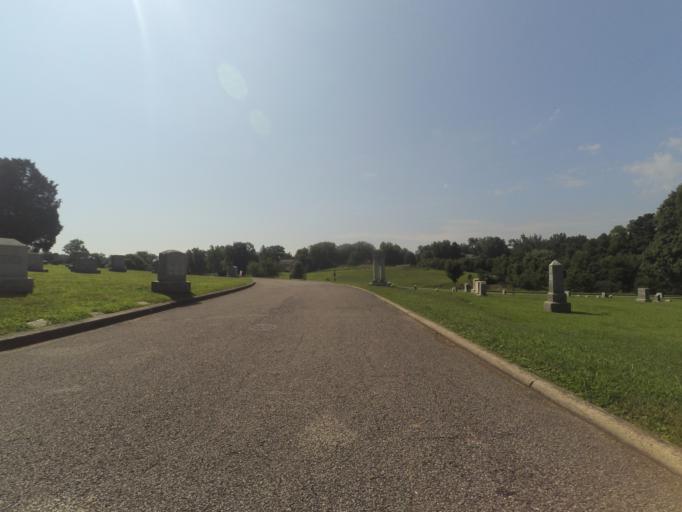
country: US
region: West Virginia
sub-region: Cabell County
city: Huntington
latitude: 38.4087
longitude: -82.4169
